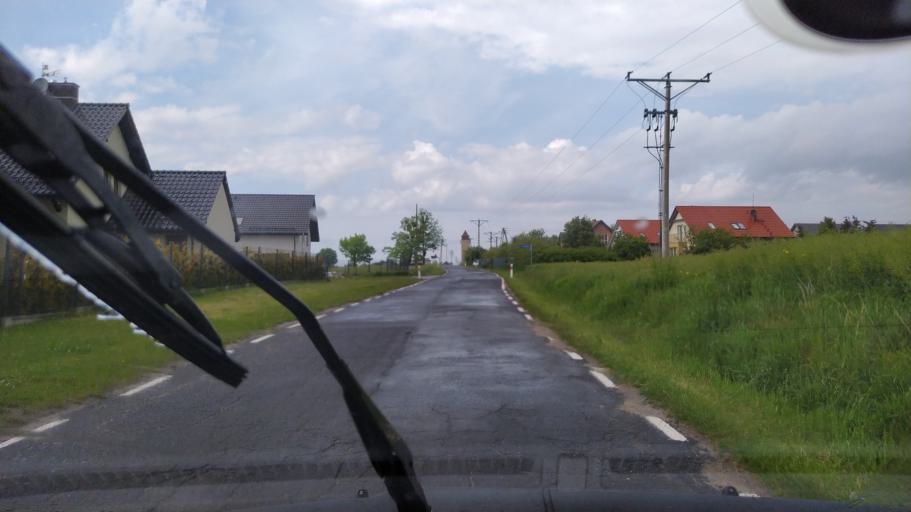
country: PL
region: Silesian Voivodeship
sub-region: Powiat gliwicki
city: Zernica
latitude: 50.2350
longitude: 18.6174
